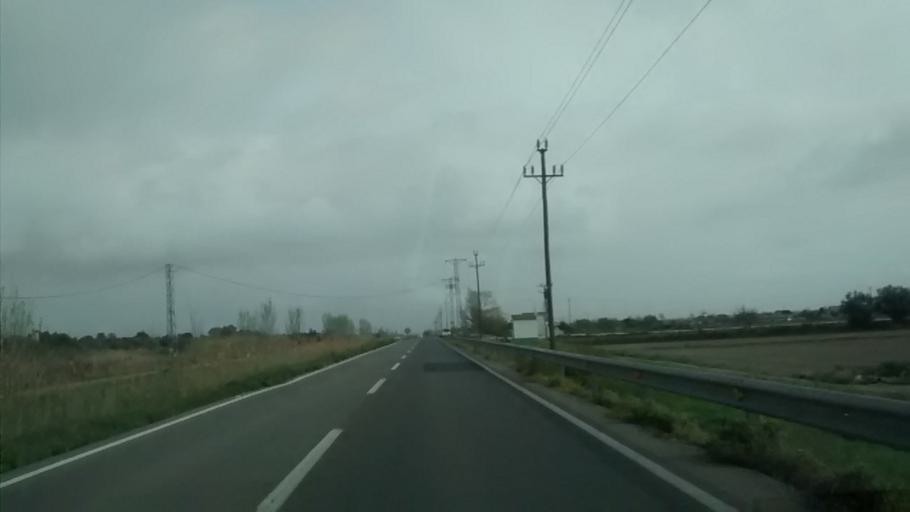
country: ES
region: Catalonia
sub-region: Provincia de Tarragona
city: Sant Carles de la Rapita
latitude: 40.6253
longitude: 0.5998
